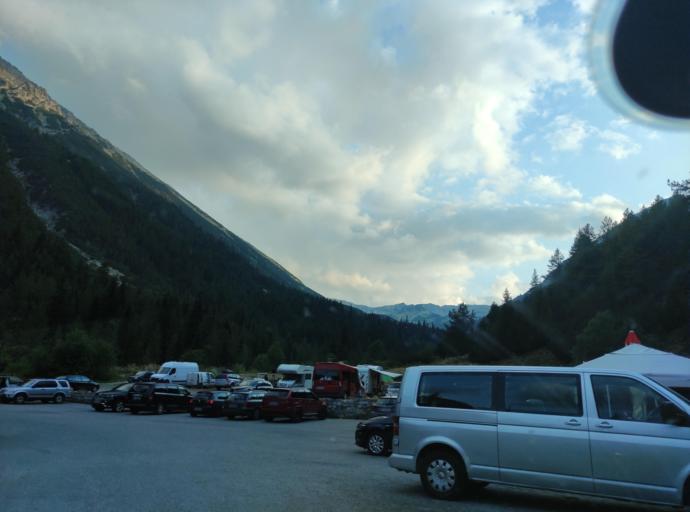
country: BG
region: Blagoevgrad
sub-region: Obshtina Bansko
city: Bansko
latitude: 41.7668
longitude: 23.4246
